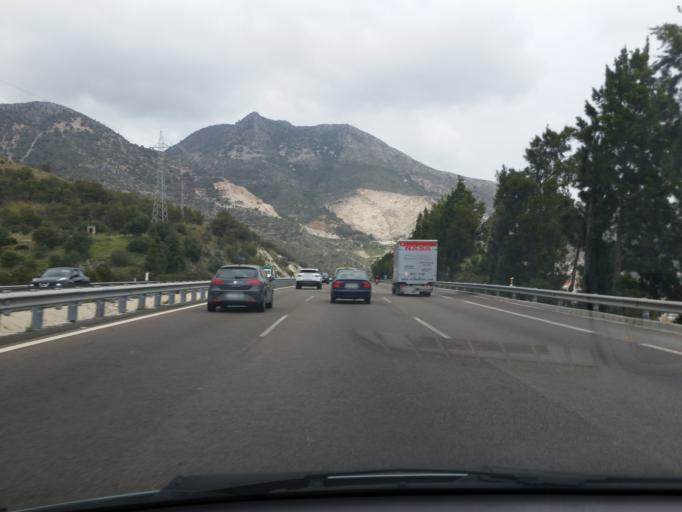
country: ES
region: Andalusia
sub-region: Provincia de Malaga
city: Benalmadena
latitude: 36.5982
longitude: -4.5743
